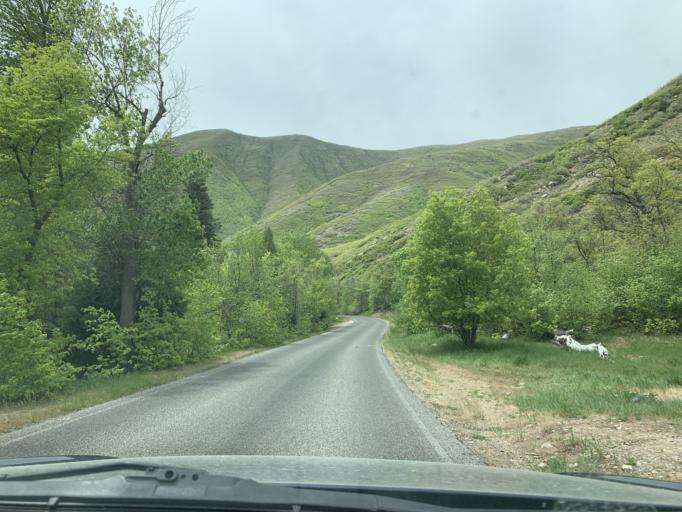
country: US
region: Utah
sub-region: Utah County
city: Mapleton
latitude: 40.1829
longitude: -111.4640
